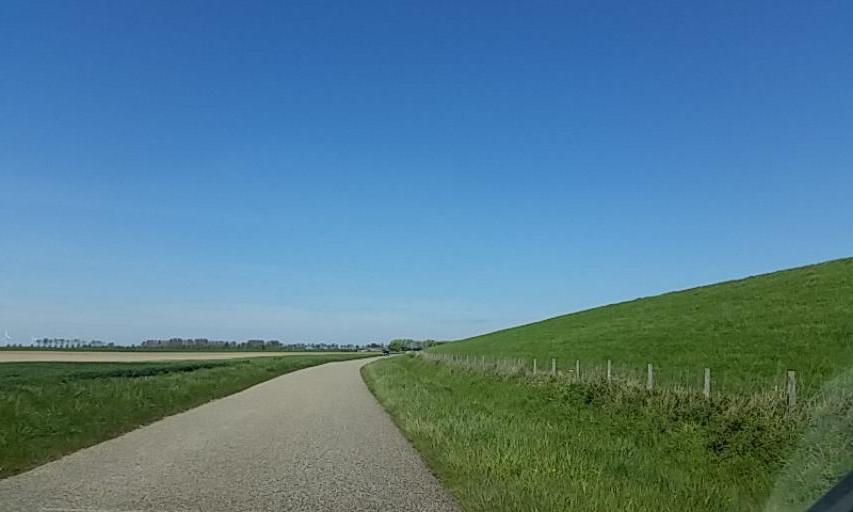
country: NL
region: Zeeland
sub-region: Gemeente Borsele
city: Borssele
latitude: 51.3575
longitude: 3.7040
